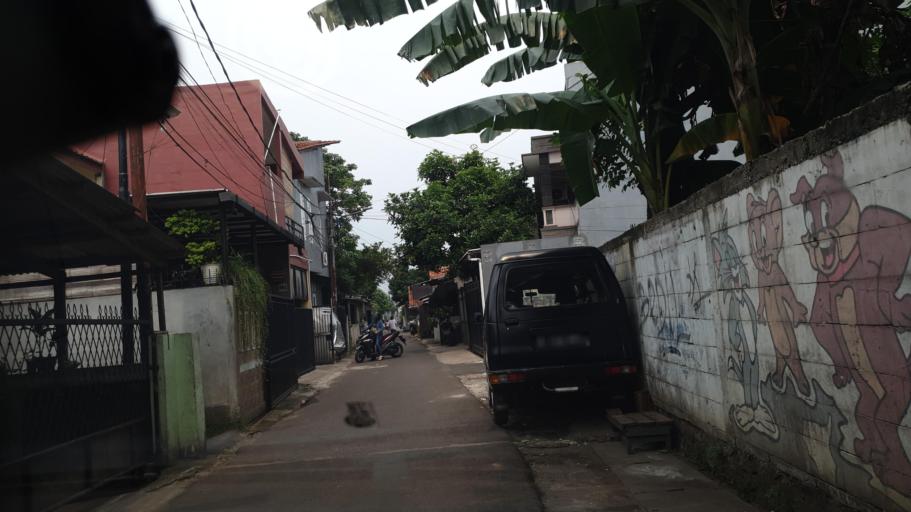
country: ID
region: West Java
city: Pamulang
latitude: -6.3322
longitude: 106.7708
